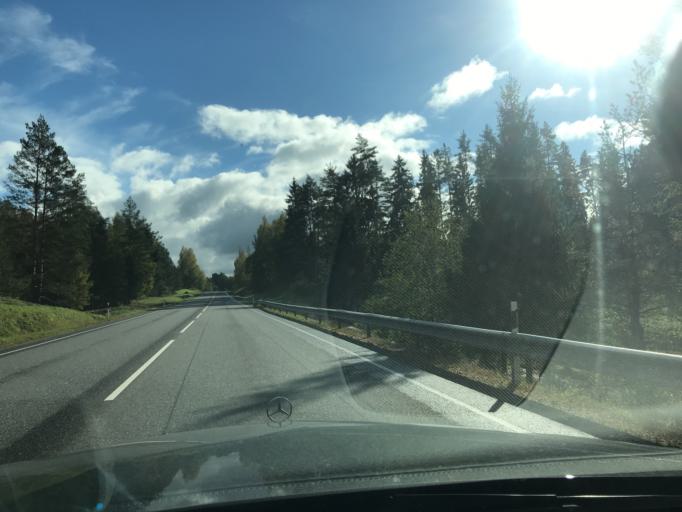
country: EE
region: Vorumaa
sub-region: Voru linn
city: Voru
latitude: 57.8021
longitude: 27.0861
